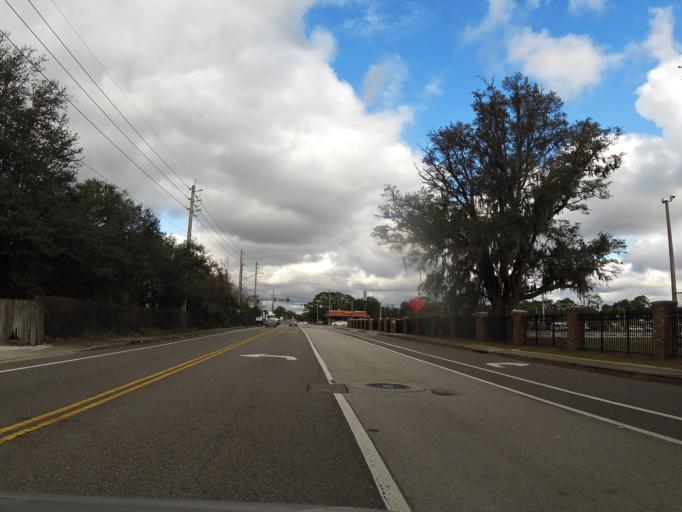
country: US
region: Florida
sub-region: Duval County
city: Jacksonville
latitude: 30.2689
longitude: -81.6101
